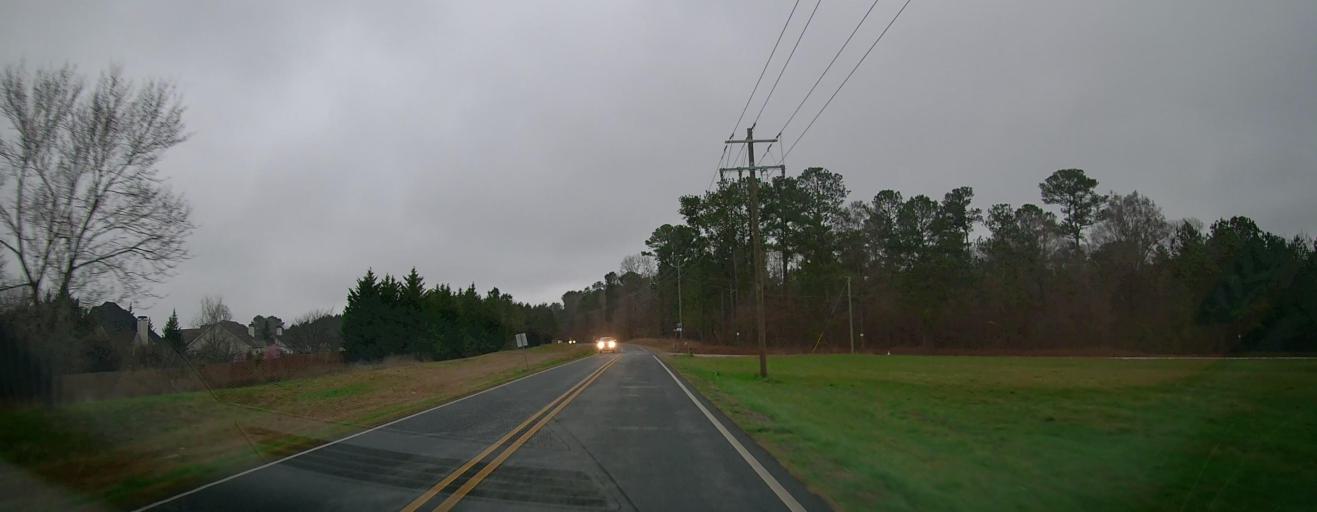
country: US
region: Georgia
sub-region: Pike County
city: Zebulon
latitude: 33.1643
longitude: -84.3579
